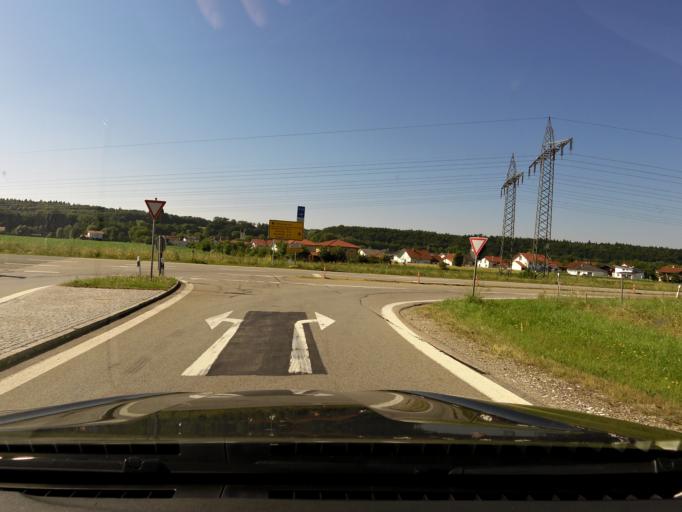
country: DE
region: Bavaria
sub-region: Upper Bavaria
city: Perach
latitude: 48.2472
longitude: 12.7519
